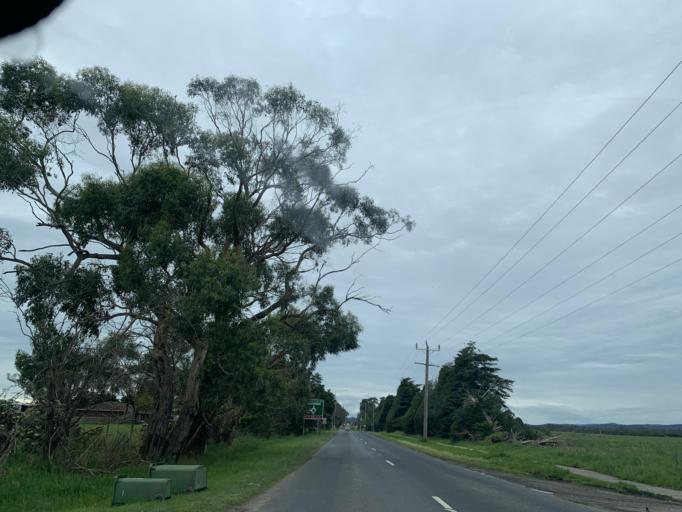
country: AU
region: Victoria
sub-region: Cardinia
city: Pakenham South
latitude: -38.0779
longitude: 145.5709
